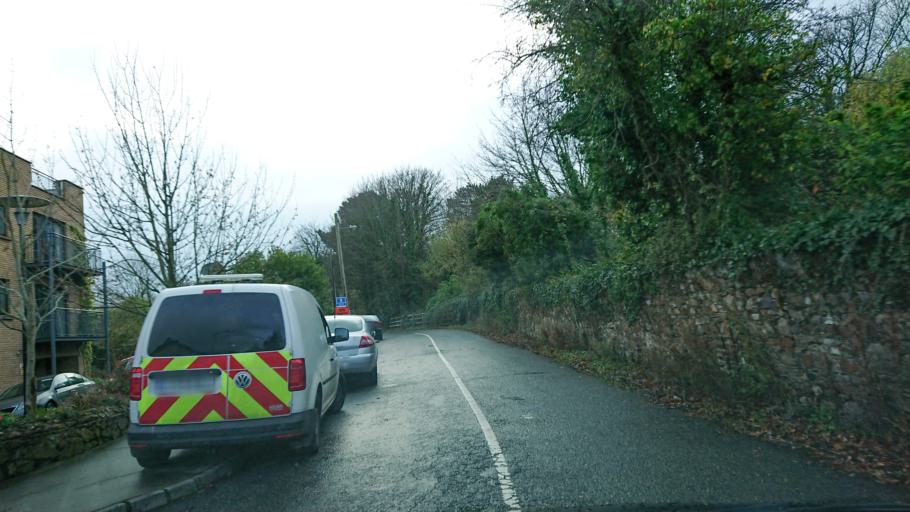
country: IE
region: Munster
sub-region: Waterford
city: Waterford
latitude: 52.2493
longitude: -7.0741
